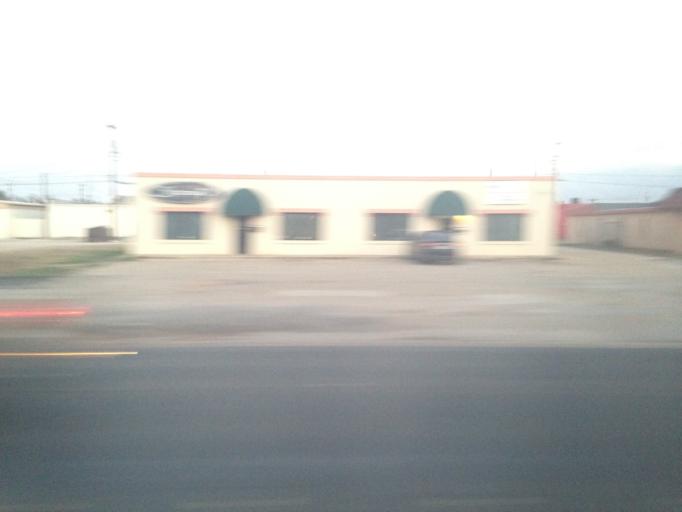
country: US
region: Texas
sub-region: Taylor County
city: Abilene
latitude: 32.4527
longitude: -99.7580
